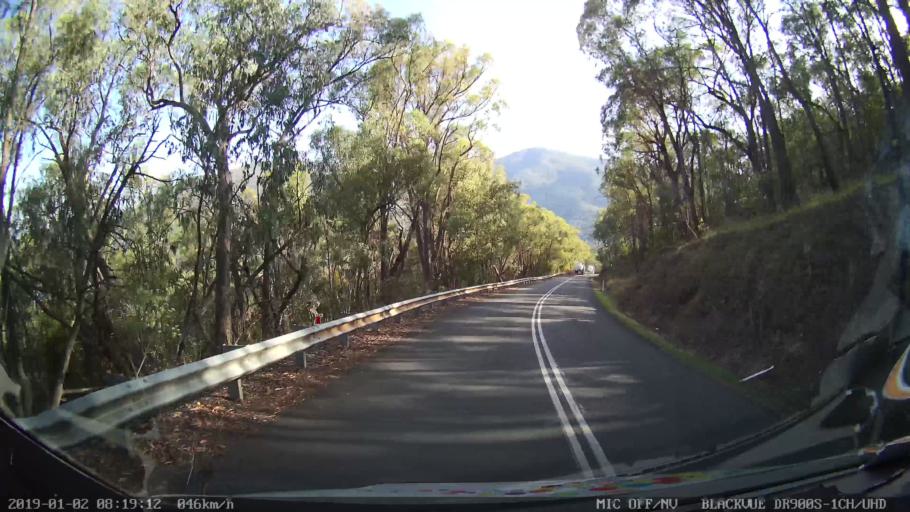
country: AU
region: New South Wales
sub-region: Tumut Shire
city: Tumut
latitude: -35.5763
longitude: 148.3201
